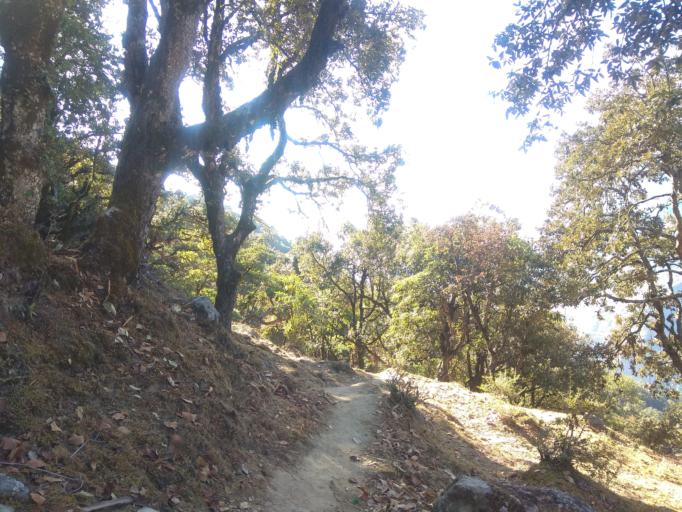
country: NP
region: Far Western
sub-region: Seti Zone
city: Achham
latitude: 29.2734
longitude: 81.6136
